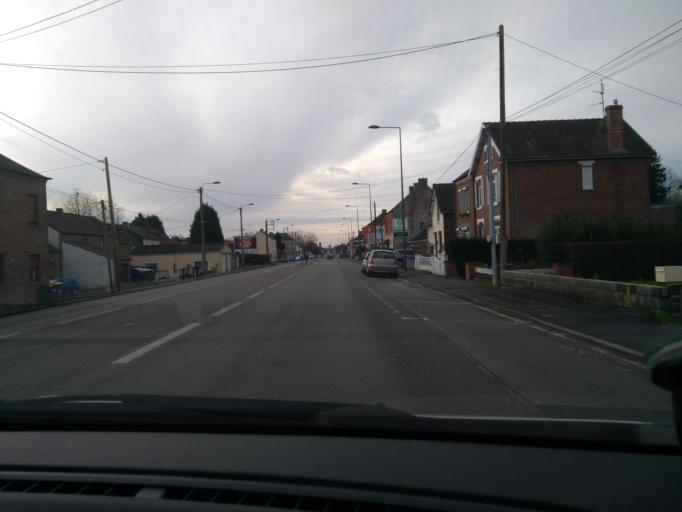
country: FR
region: Nord-Pas-de-Calais
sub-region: Departement du Nord
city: Maubeuge
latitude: 50.3003
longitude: 3.9774
